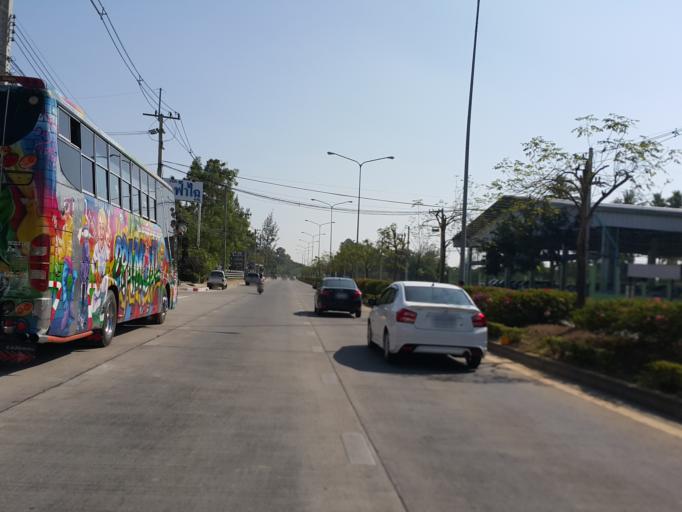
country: TH
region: Chiang Mai
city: San Sai
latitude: 18.8335
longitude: 99.0037
